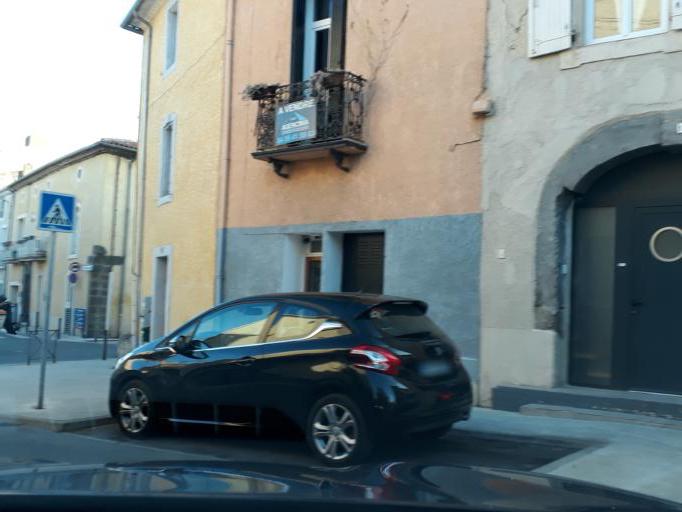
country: FR
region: Languedoc-Roussillon
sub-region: Departement de l'Herault
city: Marseillan
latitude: 43.3557
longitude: 3.5295
